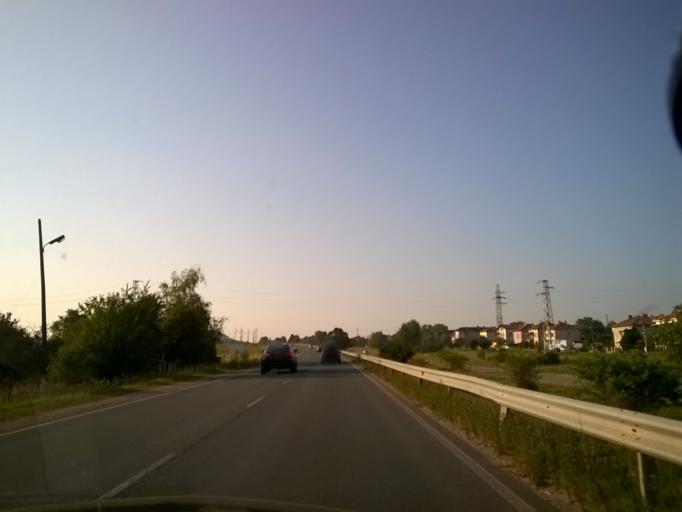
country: BG
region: Sofiya
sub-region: Obshtina Dragoman
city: Dragoman
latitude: 42.9166
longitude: 22.9395
